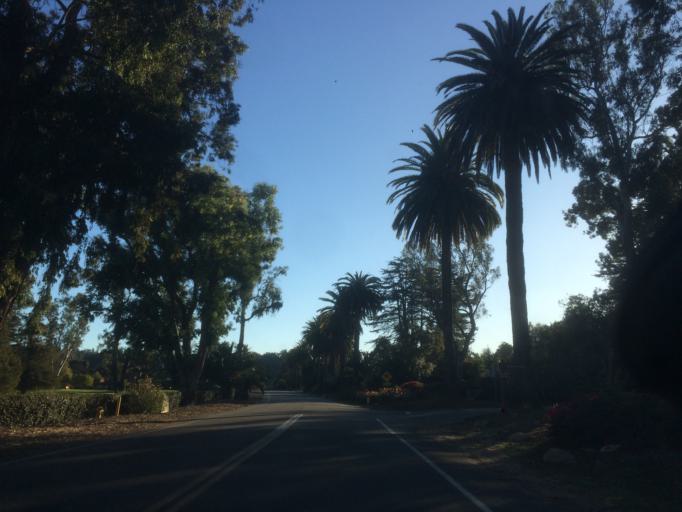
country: US
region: California
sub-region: Santa Barbara County
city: Mission Canyon
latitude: 34.4323
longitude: -119.7622
